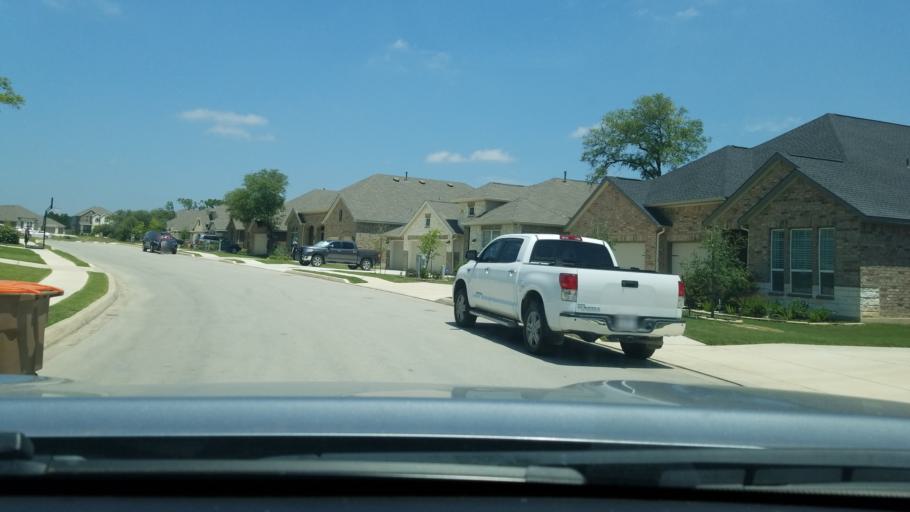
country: US
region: Texas
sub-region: Comal County
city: Bulverde
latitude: 29.8038
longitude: -98.5176
